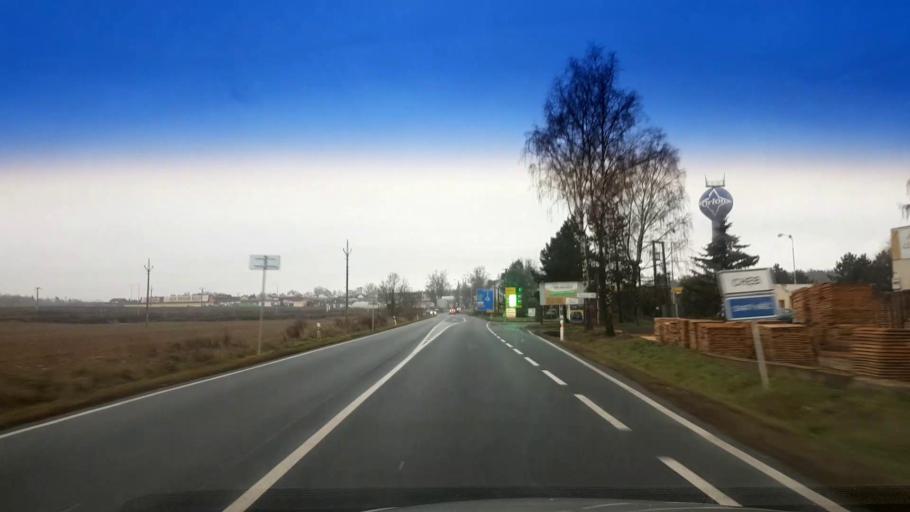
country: CZ
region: Karlovarsky
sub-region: Okres Cheb
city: Cheb
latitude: 50.0523
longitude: 12.3554
